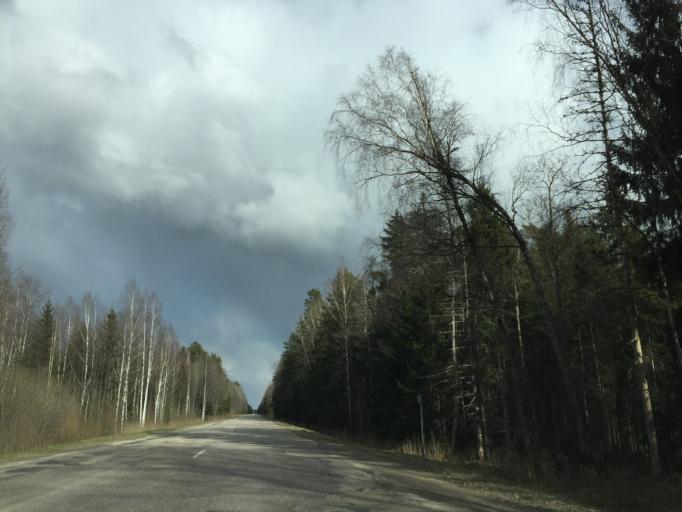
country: LV
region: Garkalne
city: Garkalne
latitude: 56.9473
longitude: 24.4739
